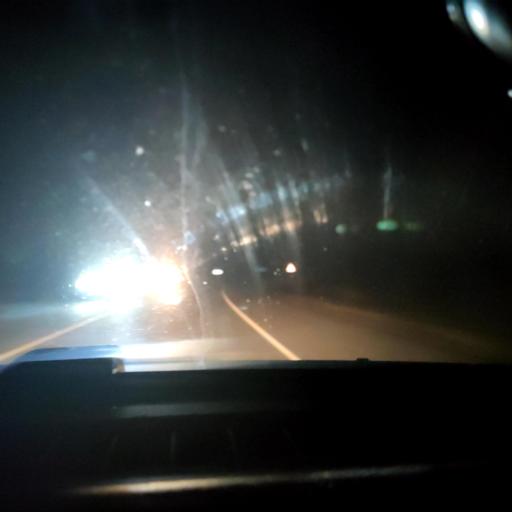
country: RU
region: Voronezj
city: Devitsa
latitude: 51.5943
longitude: 38.9776
